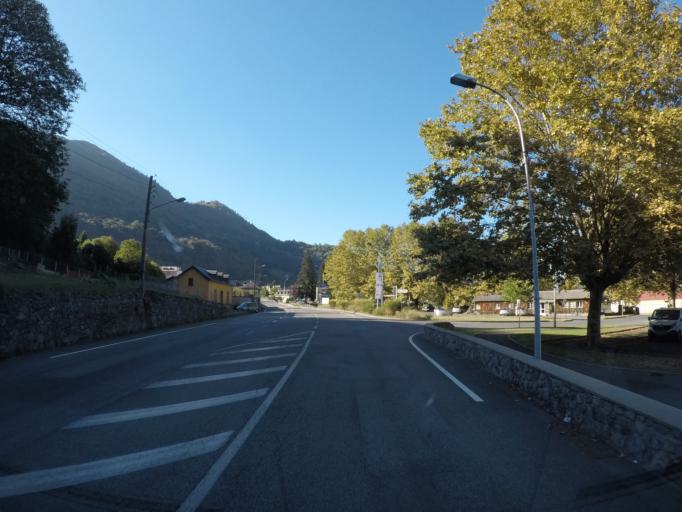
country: FR
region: Midi-Pyrenees
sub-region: Departement des Hautes-Pyrenees
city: Pierrefitte-Nestalas
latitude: 42.9544
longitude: -0.0710
